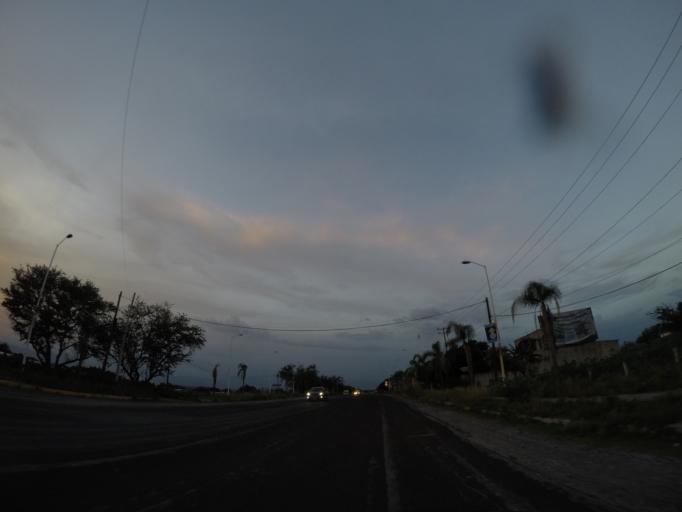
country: MX
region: Morelos
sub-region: Jojutla
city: Tehuixtla
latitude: 18.5904
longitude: -99.2592
